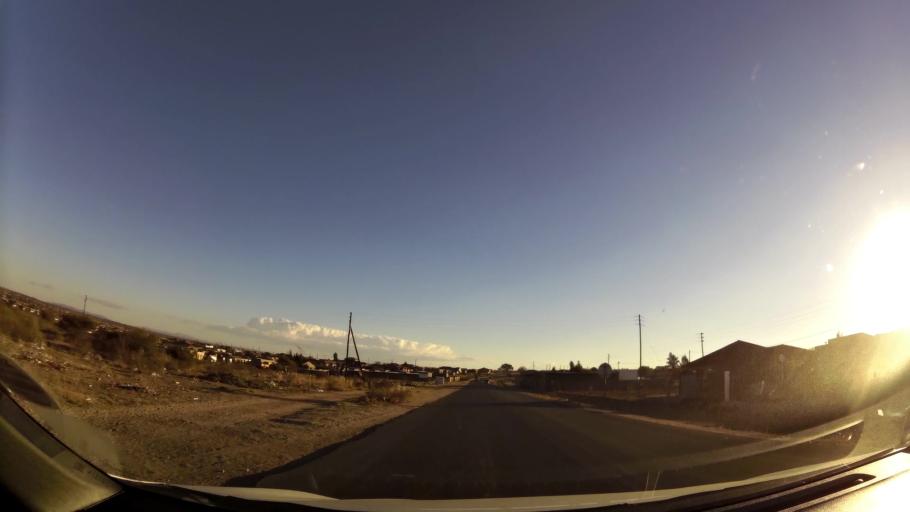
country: ZA
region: Limpopo
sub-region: Capricorn District Municipality
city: Polokwane
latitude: -23.8346
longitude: 29.3656
